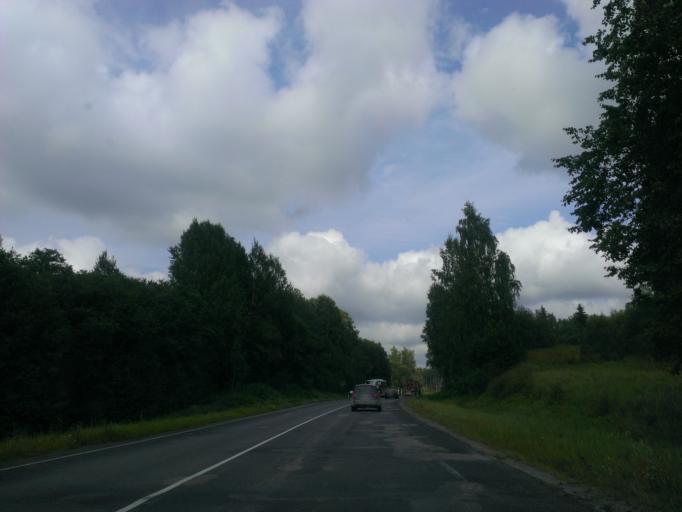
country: LV
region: Amatas Novads
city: Drabesi
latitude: 57.2525
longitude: 25.3394
